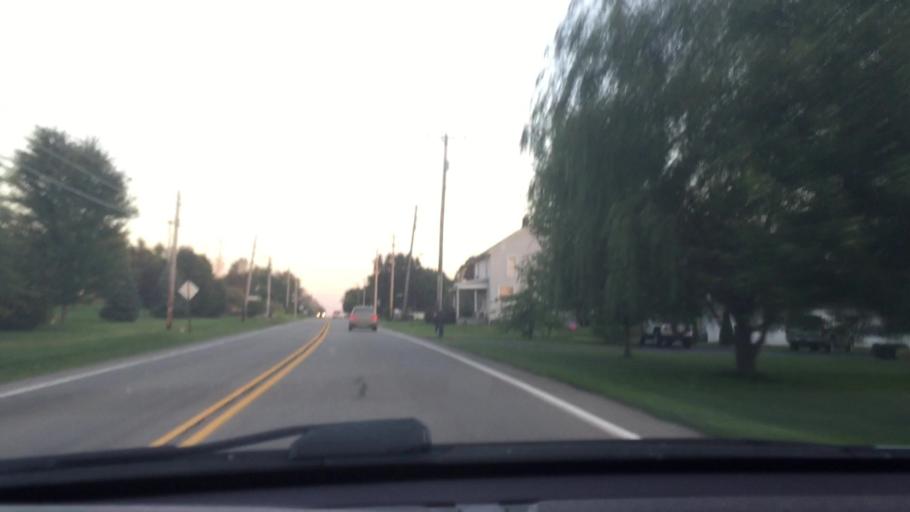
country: US
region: Pennsylvania
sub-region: Mercer County
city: Grove City
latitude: 41.1430
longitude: -80.0808
